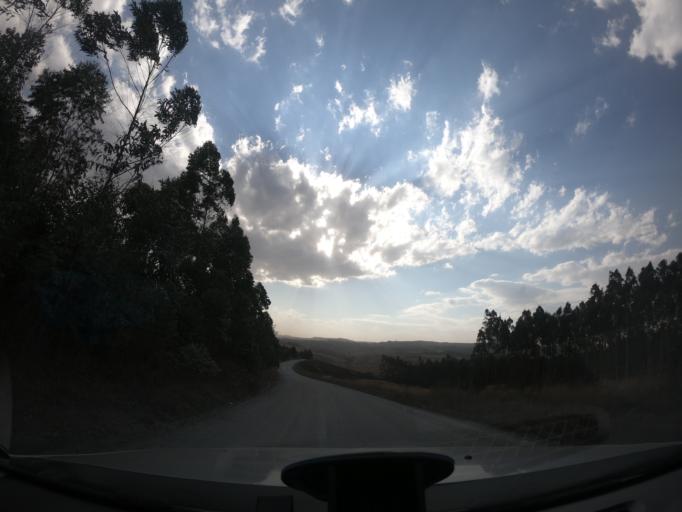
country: ZA
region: KwaZulu-Natal
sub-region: uMgungundlovu District Municipality
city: Howick
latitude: -29.4219
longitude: 30.1039
